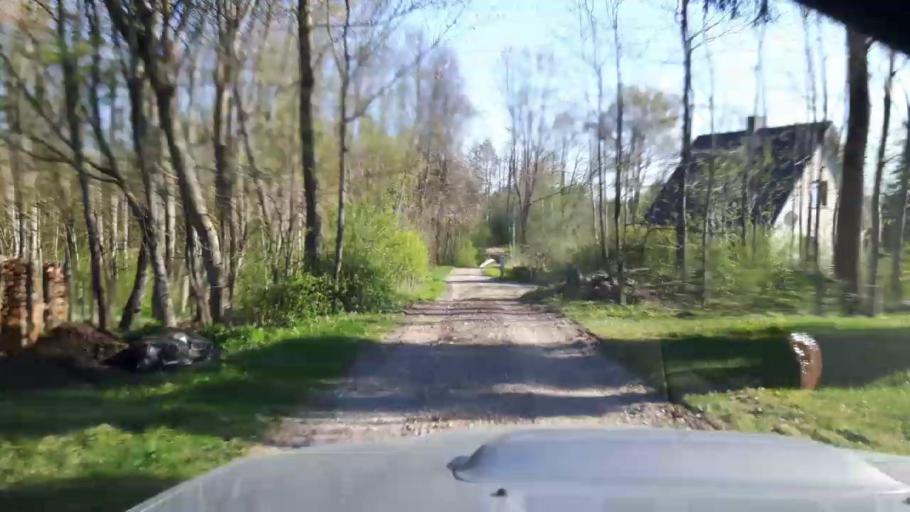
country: EE
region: Paernumaa
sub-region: Tootsi vald
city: Tootsi
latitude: 58.4838
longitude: 24.8260
